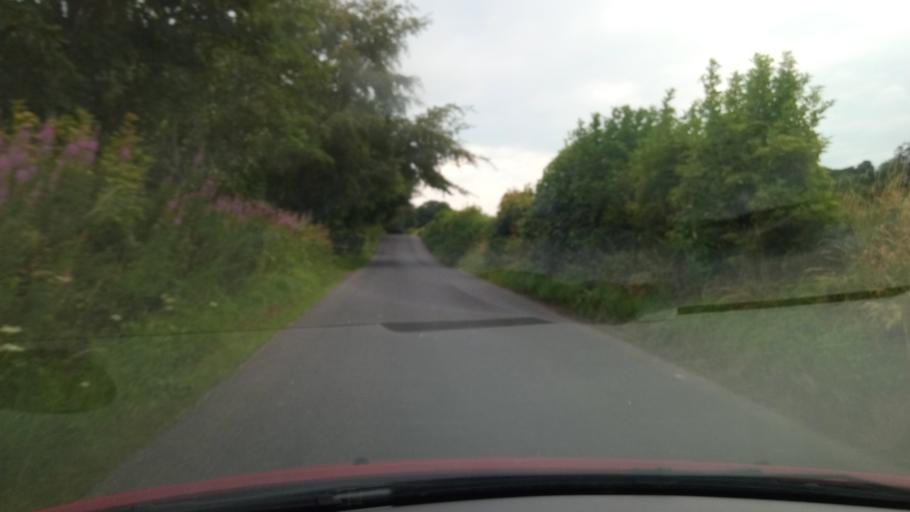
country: GB
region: Scotland
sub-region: The Scottish Borders
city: Jedburgh
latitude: 55.5181
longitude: -2.5451
